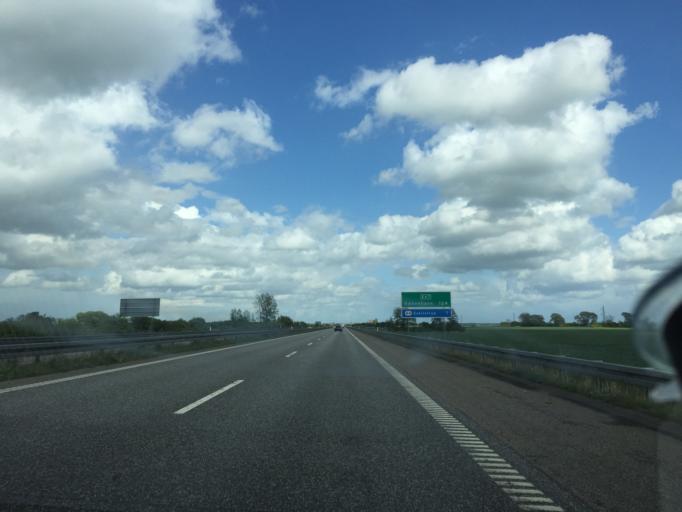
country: DK
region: Zealand
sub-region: Guldborgsund Kommune
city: Sundby
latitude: 54.8285
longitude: 11.7536
